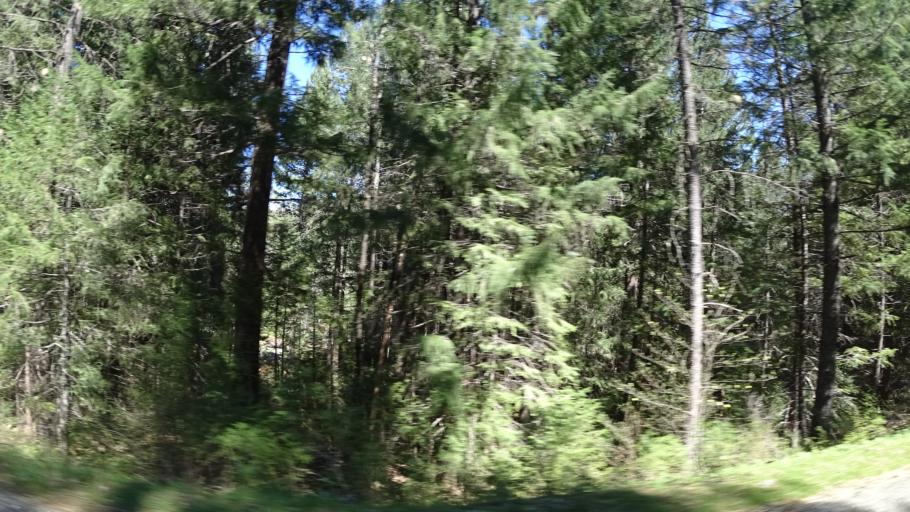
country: US
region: California
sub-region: Trinity County
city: Lewiston
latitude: 40.9121
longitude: -122.7738
